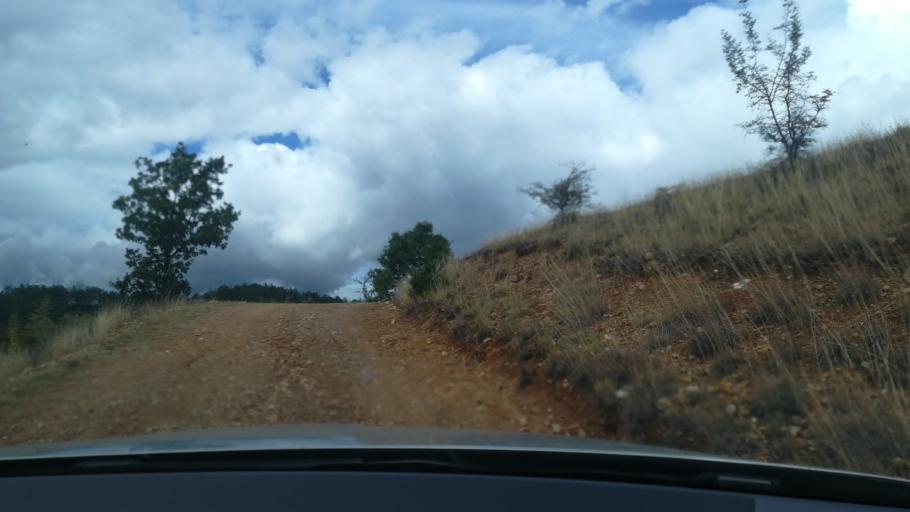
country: MK
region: Makedonska Kamenica
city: Makedonska Kamenica
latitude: 42.0049
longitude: 22.6084
